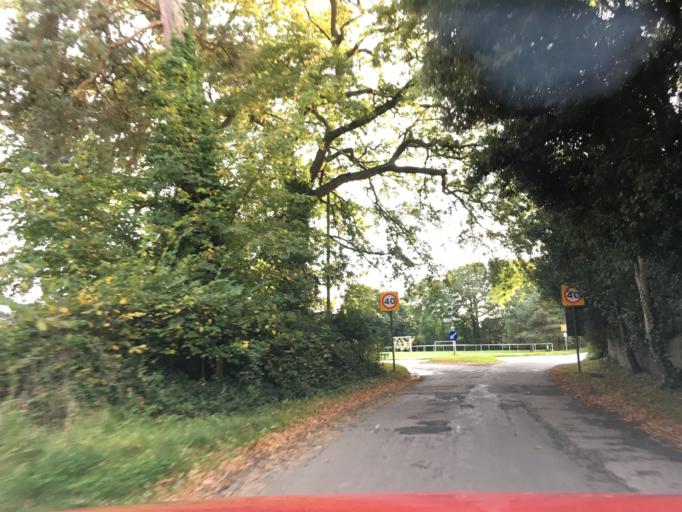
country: GB
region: England
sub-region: South Gloucestershire
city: Alveston
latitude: 51.5836
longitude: -2.5617
